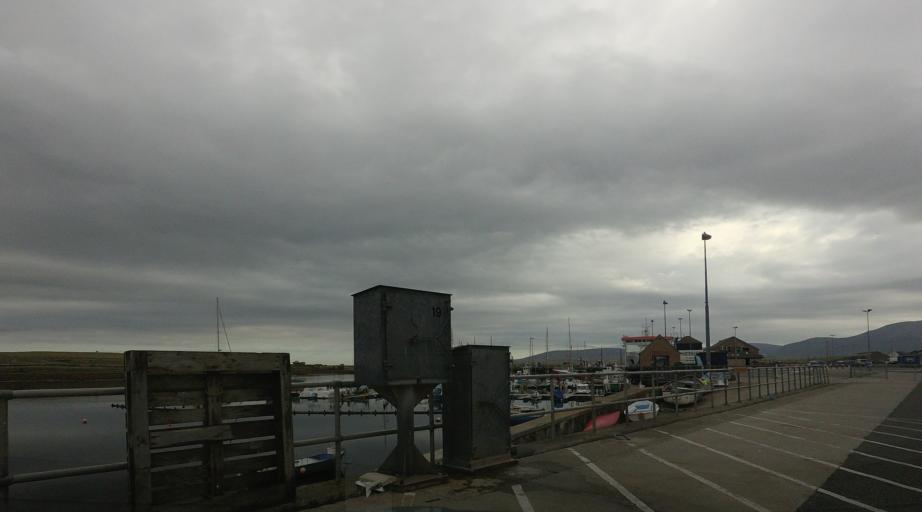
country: GB
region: Scotland
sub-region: Orkney Islands
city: Stromness
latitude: 58.9656
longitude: -3.2952
